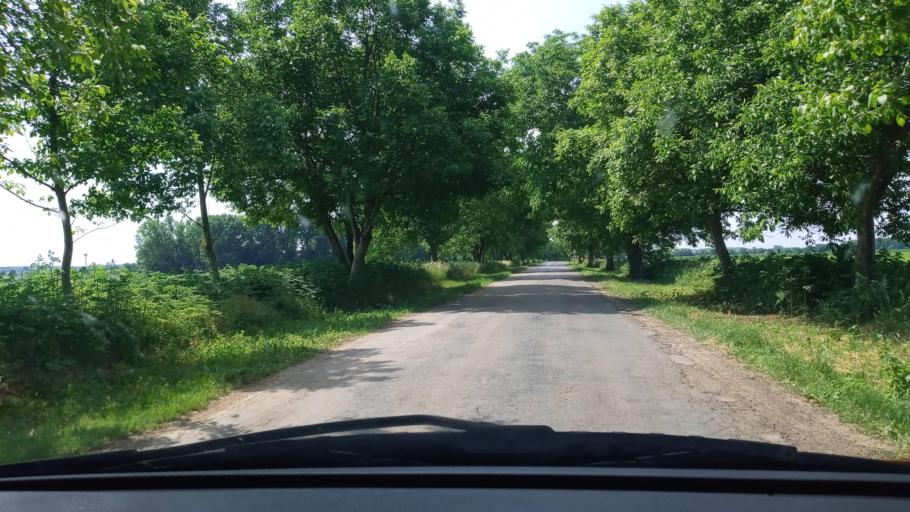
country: HU
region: Baranya
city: Szentlorinc
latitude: 46.0032
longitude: 18.0379
